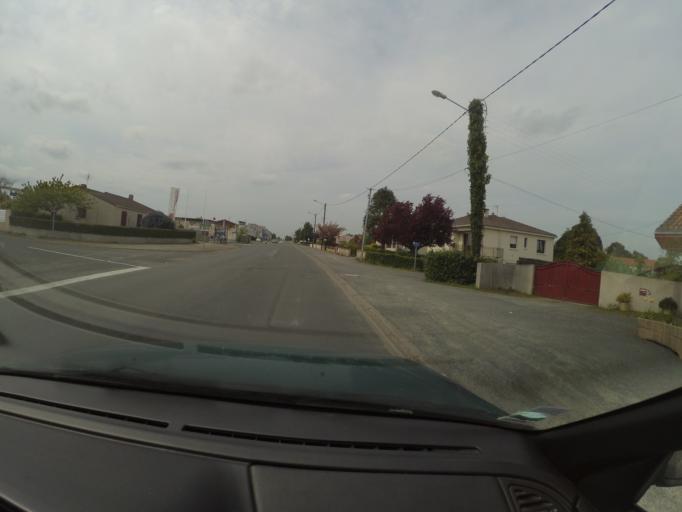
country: FR
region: Pays de la Loire
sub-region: Departement de la Loire-Atlantique
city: Gorges
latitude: 47.0944
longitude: -1.2909
